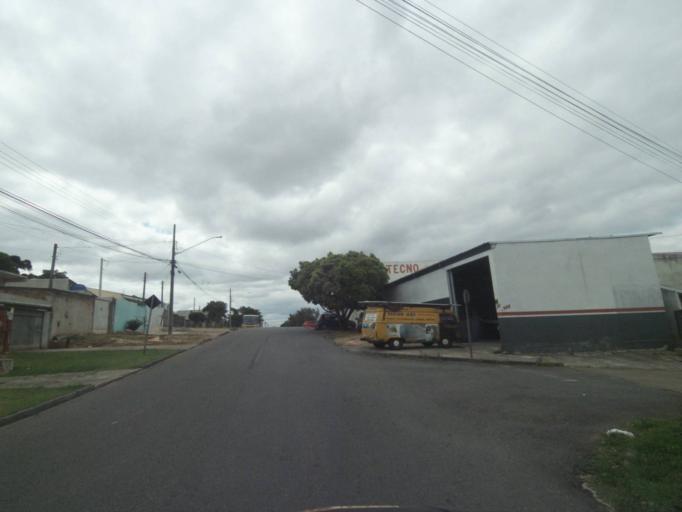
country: BR
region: Parana
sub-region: Sao Jose Dos Pinhais
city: Sao Jose dos Pinhais
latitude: -25.5567
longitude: -49.2574
